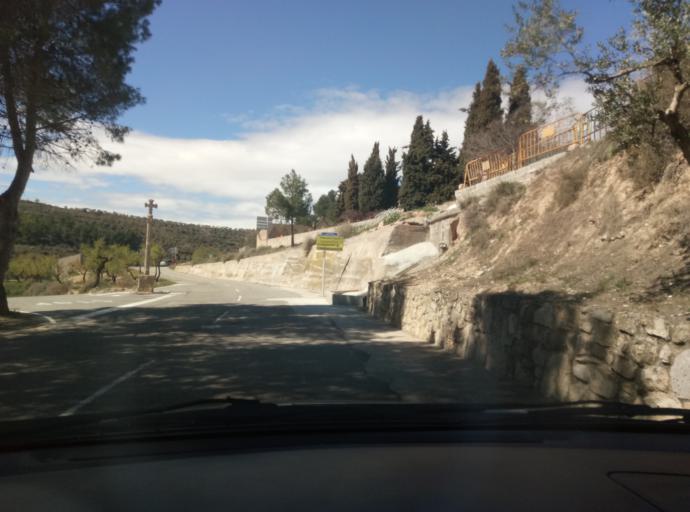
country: ES
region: Catalonia
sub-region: Provincia de Lleida
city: Vallbona de les Monges
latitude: 41.5272
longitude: 1.0861
